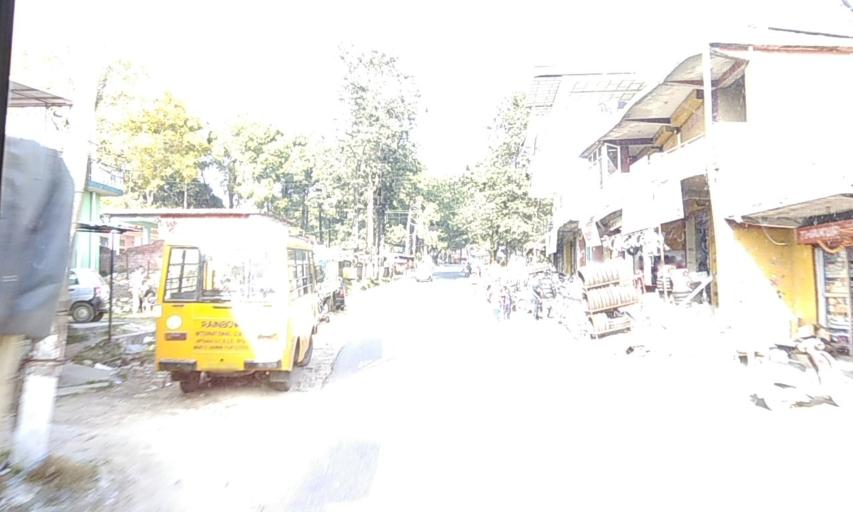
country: IN
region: Himachal Pradesh
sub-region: Kangra
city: Palampur
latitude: 32.0871
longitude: 76.5245
